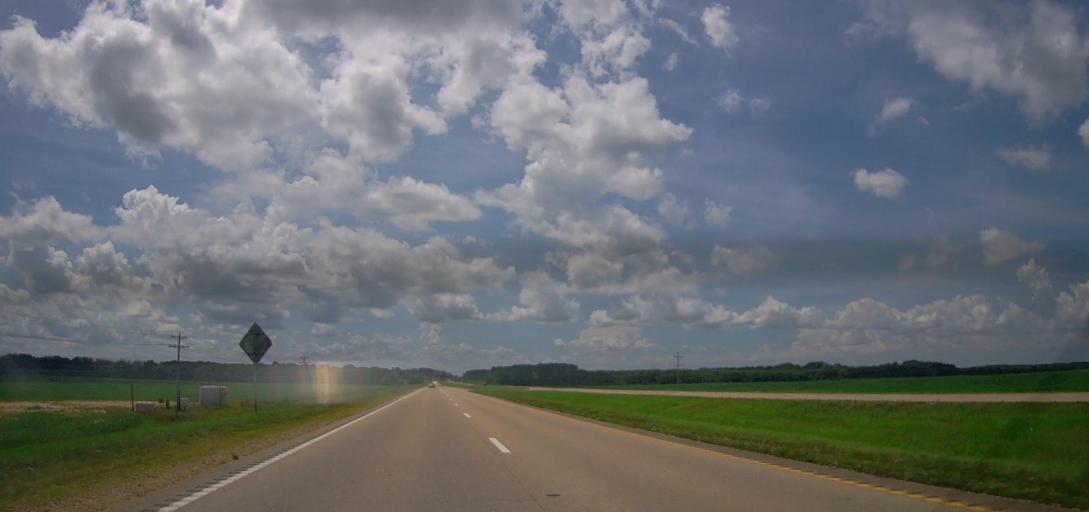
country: US
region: Mississippi
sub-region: Lee County
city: Nettleton
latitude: 34.1008
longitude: -88.6560
